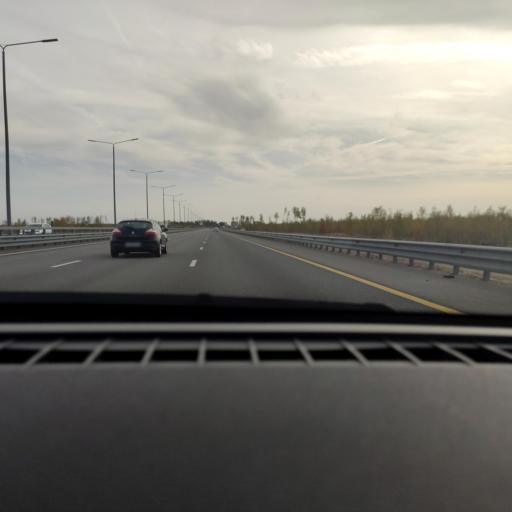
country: RU
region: Voronezj
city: Somovo
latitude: 51.7702
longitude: 39.3026
